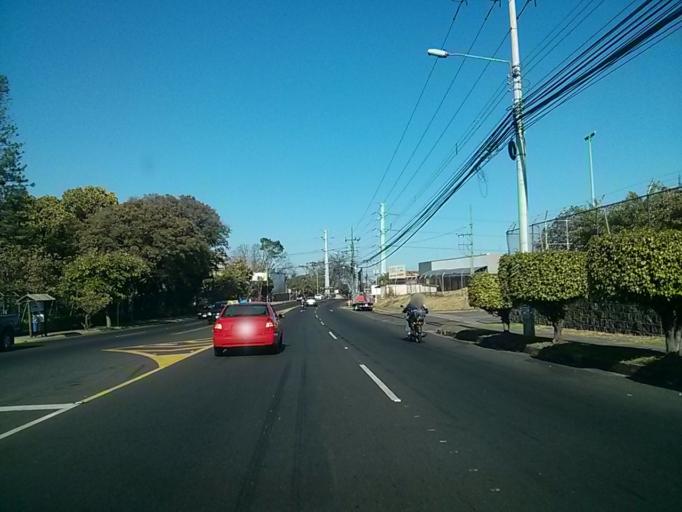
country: CR
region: Heredia
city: La Asuncion
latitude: 9.9798
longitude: -84.1659
